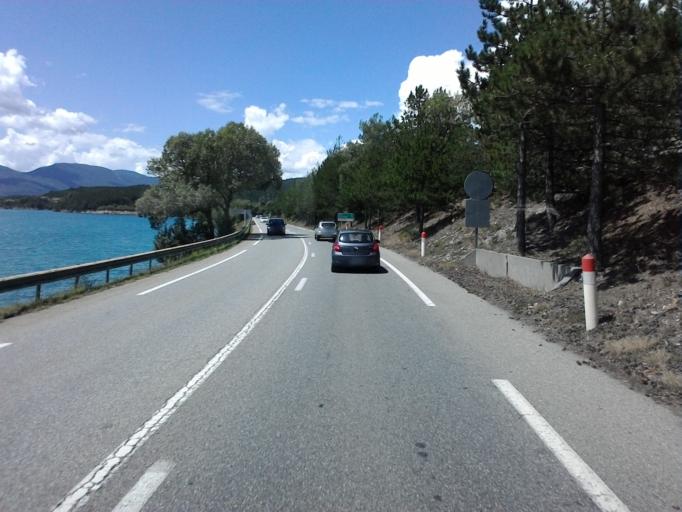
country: FR
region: Provence-Alpes-Cote d'Azur
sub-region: Departement des Hautes-Alpes
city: Embrun
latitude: 44.5356
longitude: 6.3903
